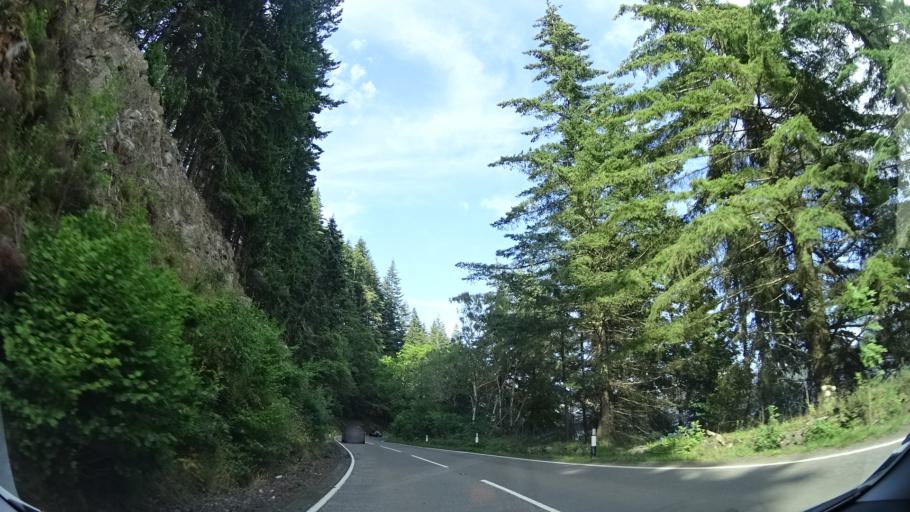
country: GB
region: Scotland
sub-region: Highland
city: Beauly
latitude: 57.2806
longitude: -4.4921
